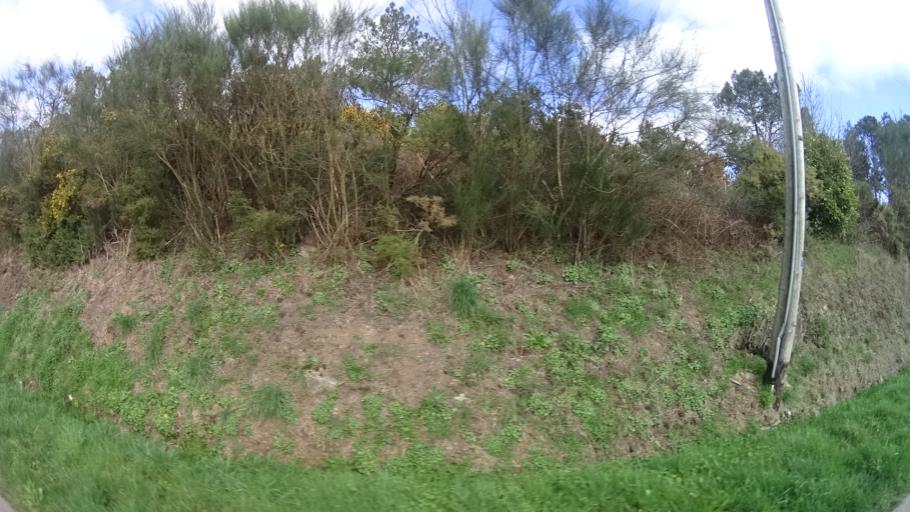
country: FR
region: Brittany
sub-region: Departement du Morbihan
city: Ruffiac
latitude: 47.8275
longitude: -2.2993
